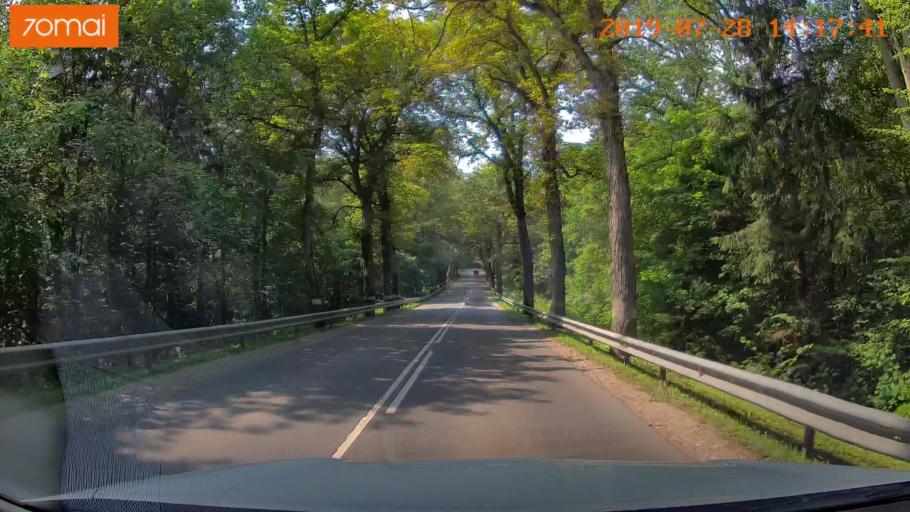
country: RU
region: Kaliningrad
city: Volochayevskoye
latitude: 54.8153
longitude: 20.2510
